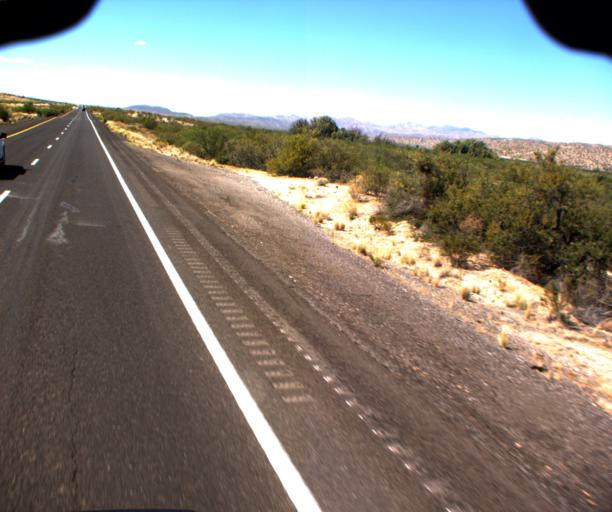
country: US
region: Arizona
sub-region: Yavapai County
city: Bagdad
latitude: 34.8417
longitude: -113.6346
